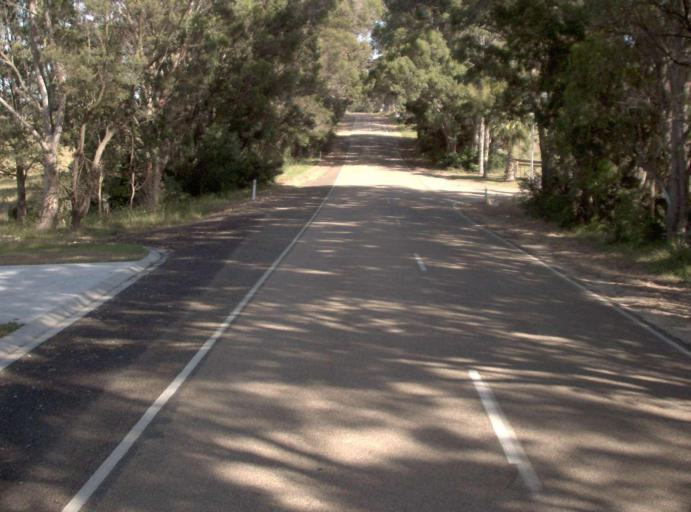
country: AU
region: Victoria
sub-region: East Gippsland
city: Lakes Entrance
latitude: -37.8198
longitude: 147.8541
